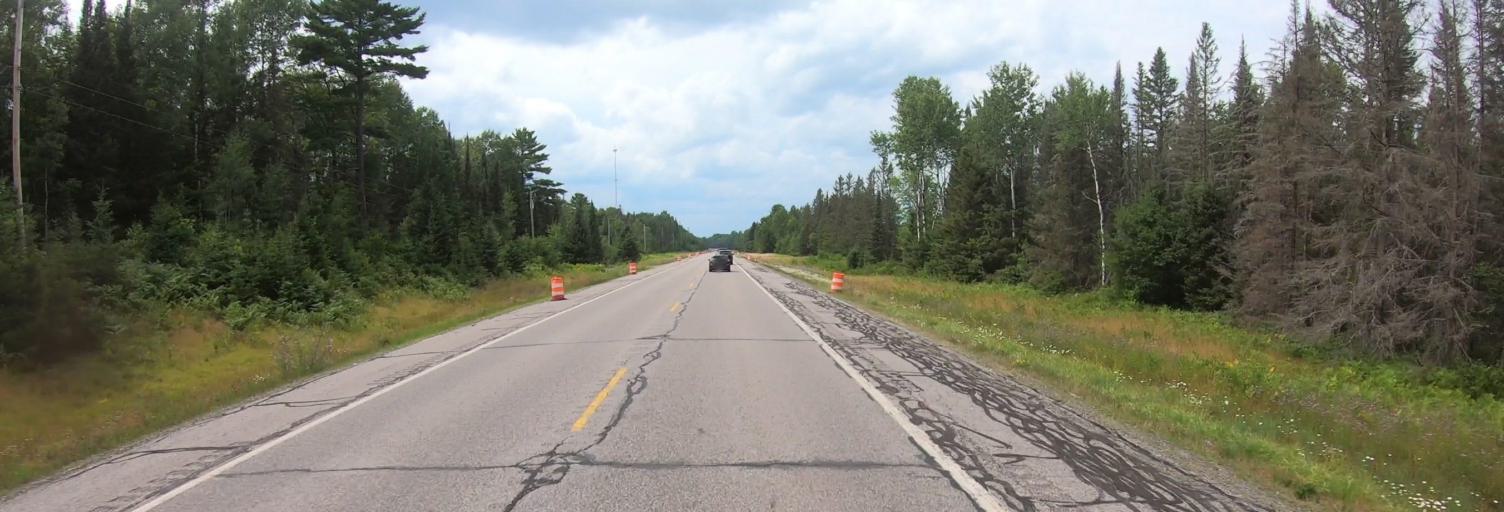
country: US
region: Michigan
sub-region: Baraga County
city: L'Anse
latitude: 46.5651
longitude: -88.2471
